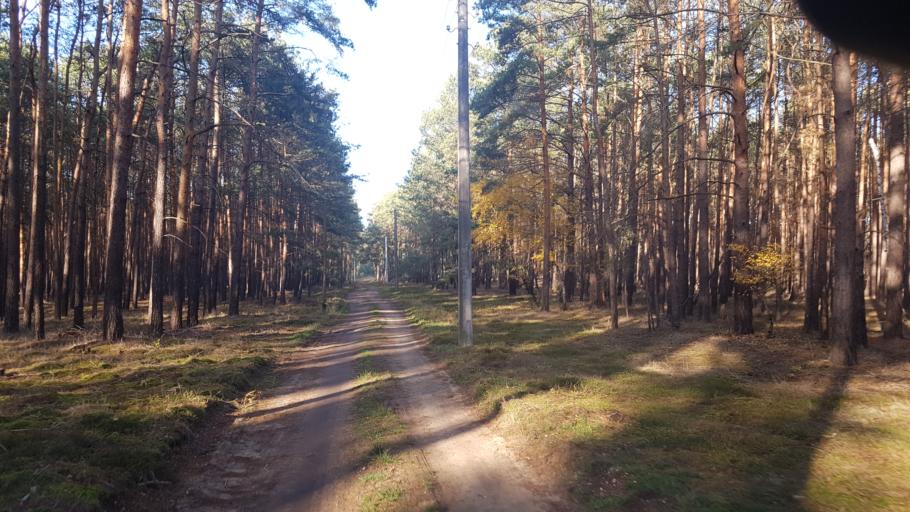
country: DE
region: Brandenburg
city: Schilda
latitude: 51.6432
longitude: 13.3494
